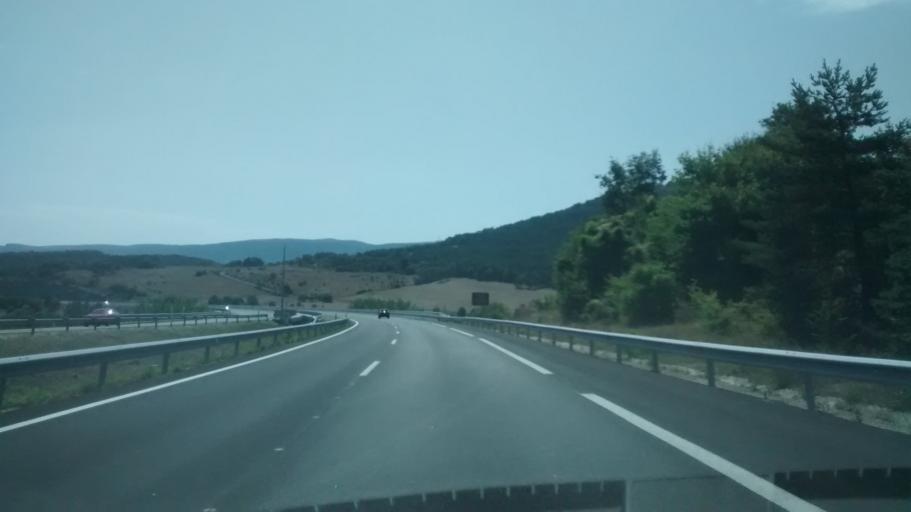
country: ES
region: Basque Country
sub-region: Provincia de Alava
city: Murguia
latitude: 42.9232
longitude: -2.9043
